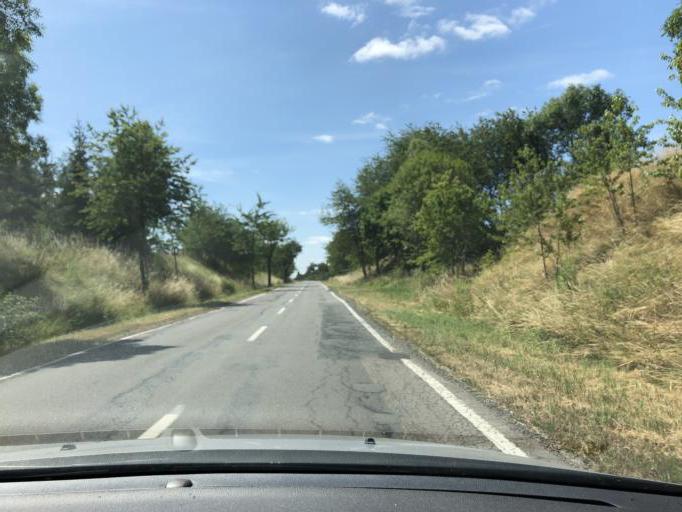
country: DE
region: Saxony-Anhalt
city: Osterfeld
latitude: 51.0618
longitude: 11.8930
